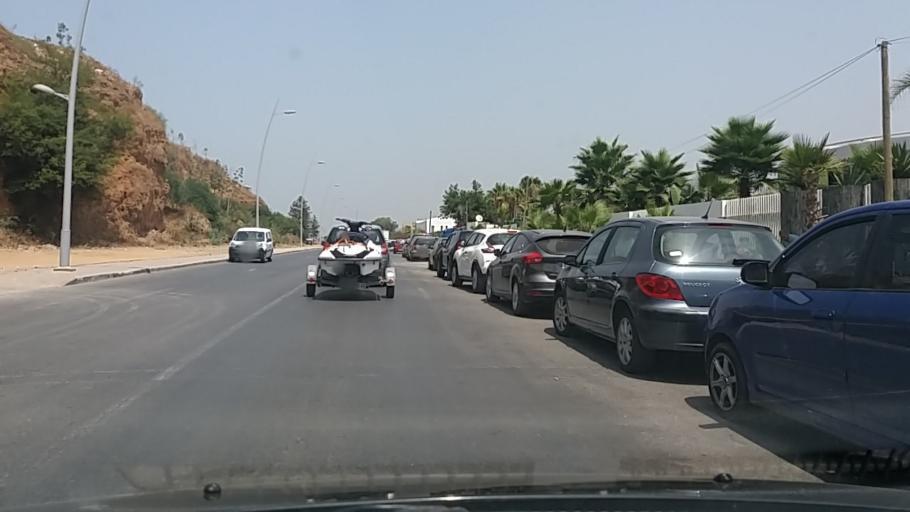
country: MA
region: Gharb-Chrarda-Beni Hssen
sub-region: Kenitra Province
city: Kenitra
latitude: 34.2700
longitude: -6.5915
